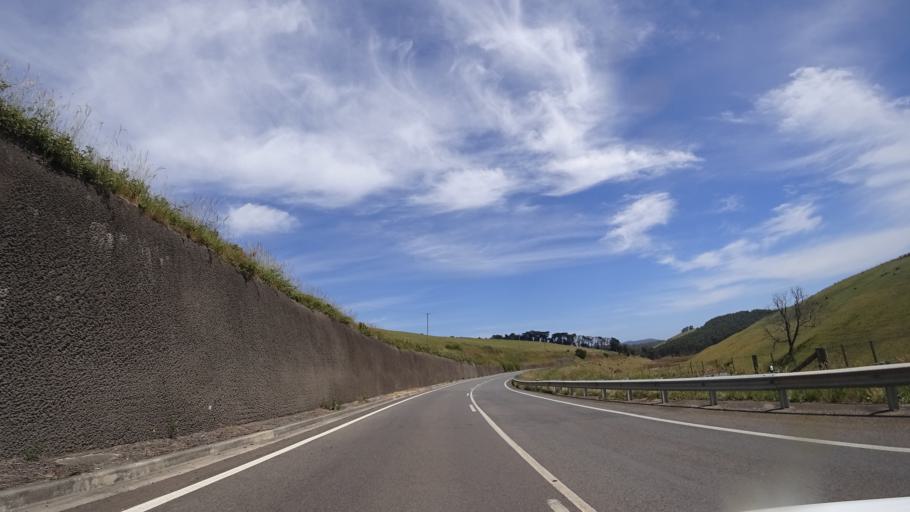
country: AU
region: Tasmania
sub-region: Dorset
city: Scottsdale
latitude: -41.1566
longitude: 147.4912
